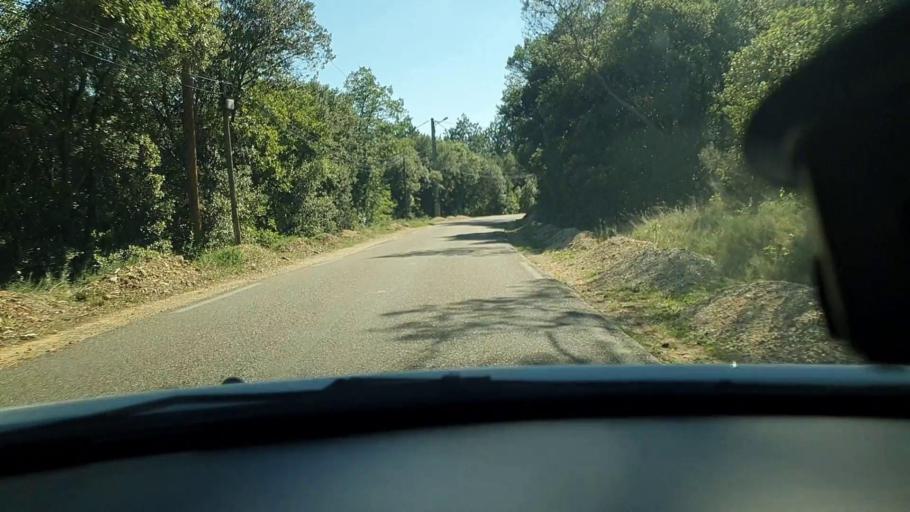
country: FR
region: Languedoc-Roussillon
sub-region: Departement du Gard
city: Sabran
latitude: 44.1902
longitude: 4.5237
